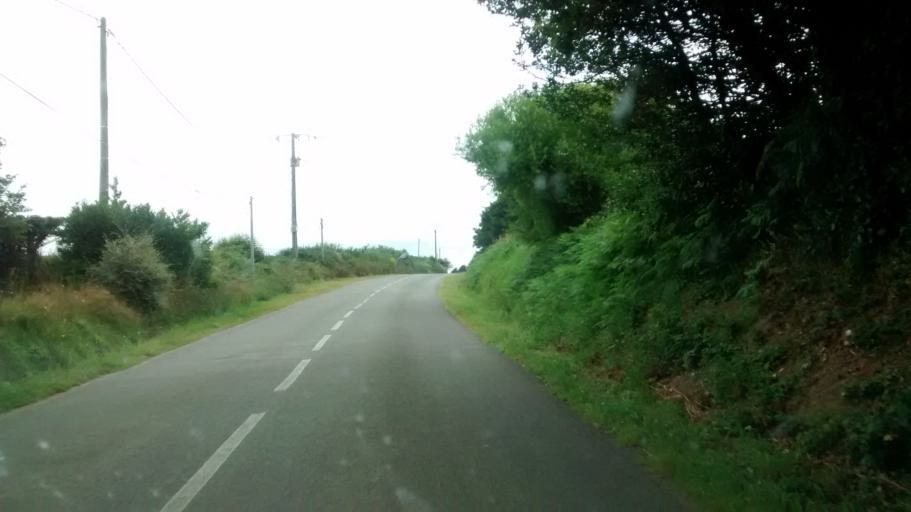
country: FR
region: Brittany
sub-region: Departement du Finistere
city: Plouedern
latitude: 48.4772
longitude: -4.2551
